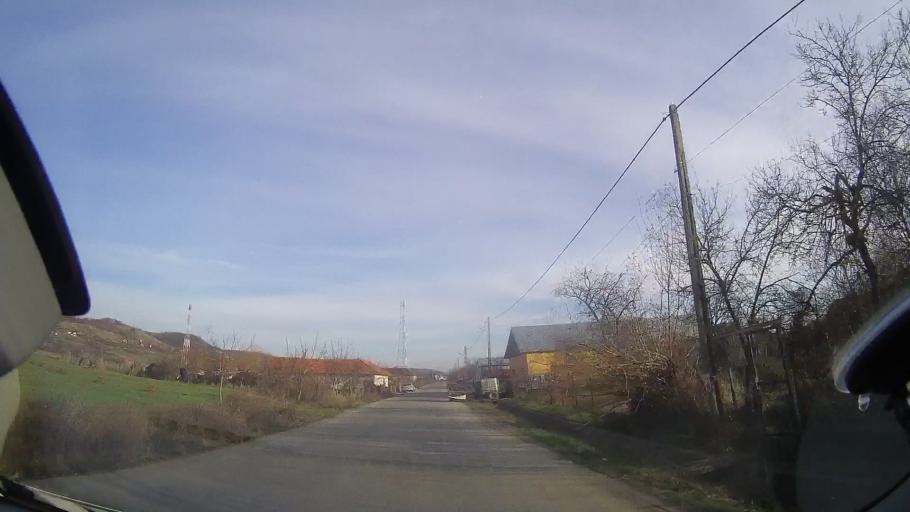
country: RO
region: Bihor
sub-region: Comuna Tileagd
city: Tileagd
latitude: 47.0824
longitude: 22.1970
